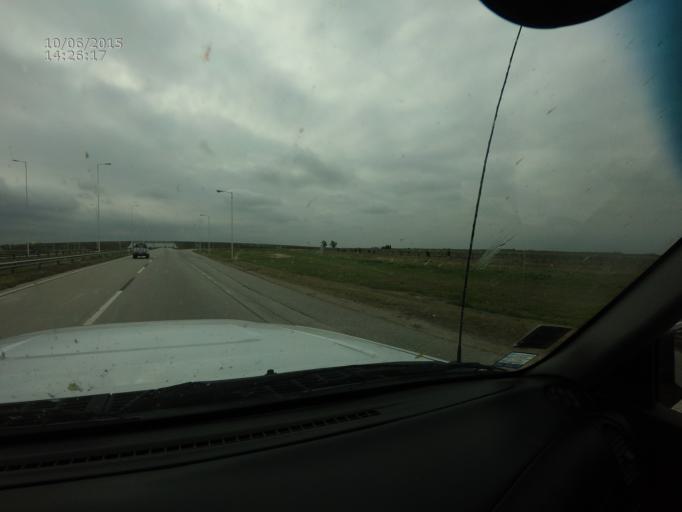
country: AR
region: Cordoba
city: Tio Pujio
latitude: -32.2579
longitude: -63.3299
